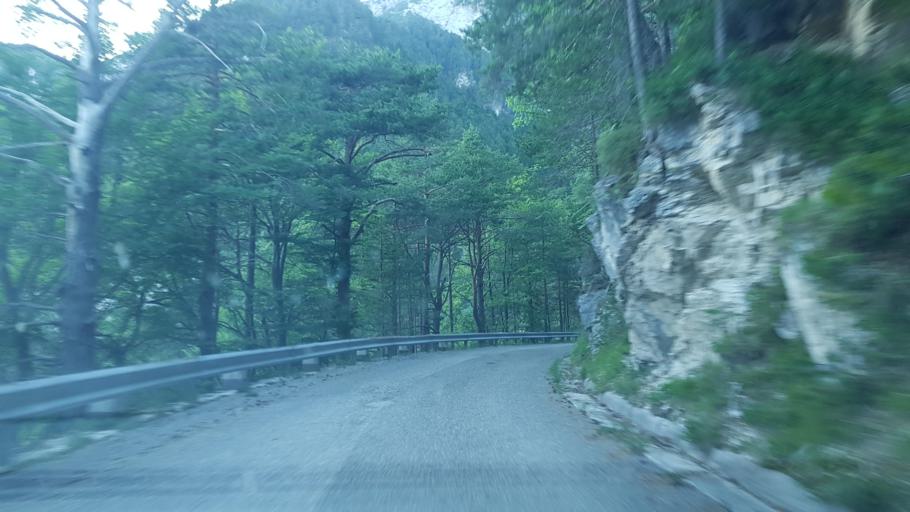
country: IT
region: Friuli Venezia Giulia
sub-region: Provincia di Udine
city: Dogna
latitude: 46.4603
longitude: 13.3839
